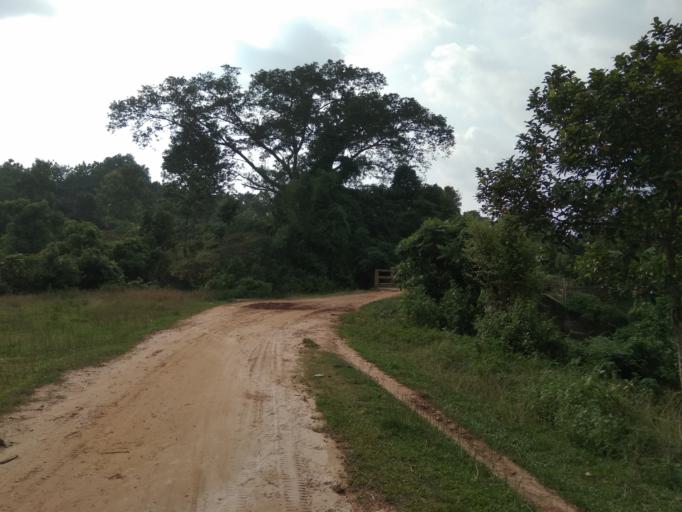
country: BD
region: Chittagong
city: Manikchari
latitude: 22.9319
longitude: 91.9108
